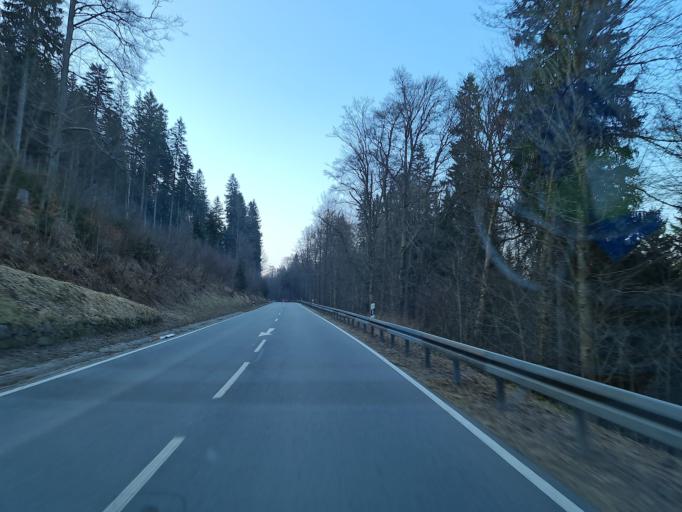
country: DE
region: Saxony
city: Sosa
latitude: 50.4669
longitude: 12.6303
